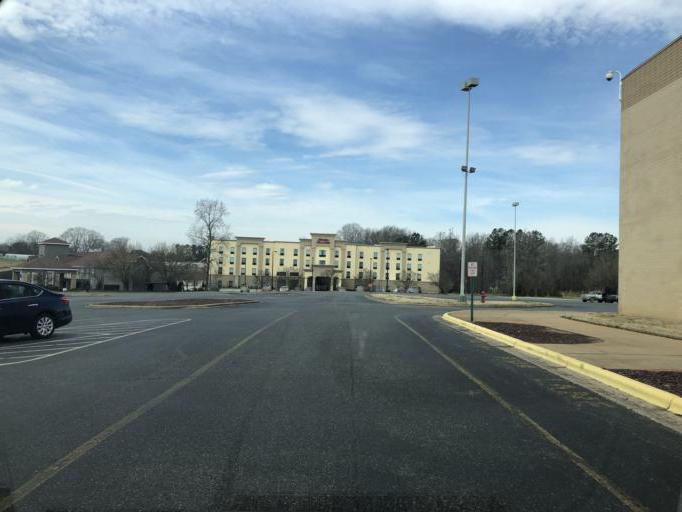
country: US
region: North Carolina
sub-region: Cleveland County
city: Shelby
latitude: 35.2696
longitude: -81.4845
